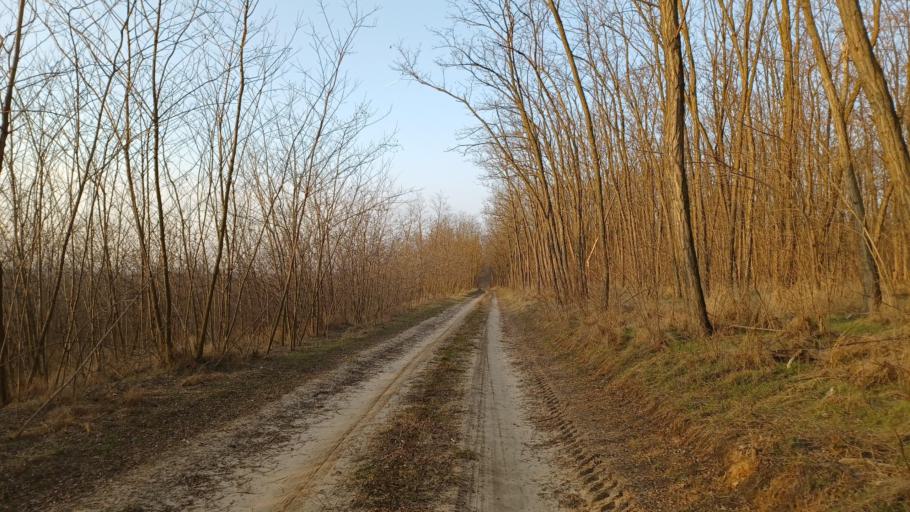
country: HU
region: Tolna
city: Tengelic
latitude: 46.5289
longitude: 18.6896
